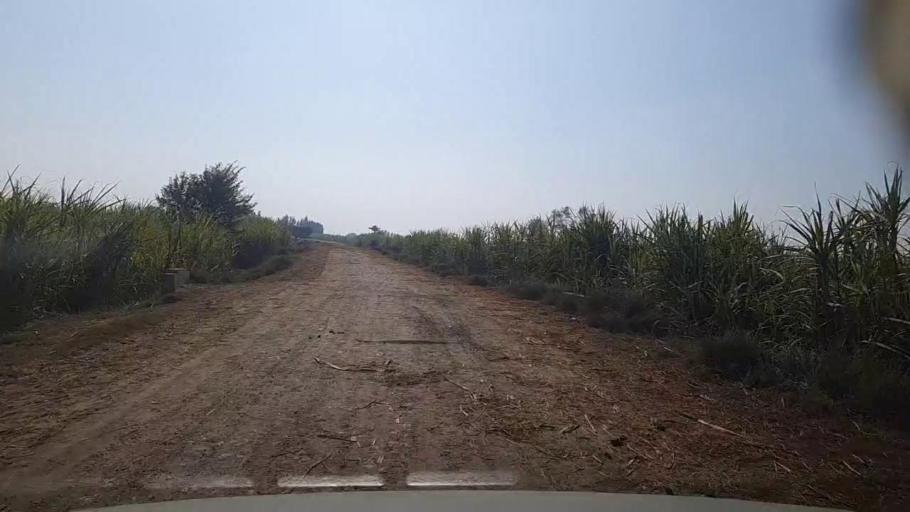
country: PK
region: Sindh
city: Mirpur Mathelo
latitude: 28.0697
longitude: 69.6173
